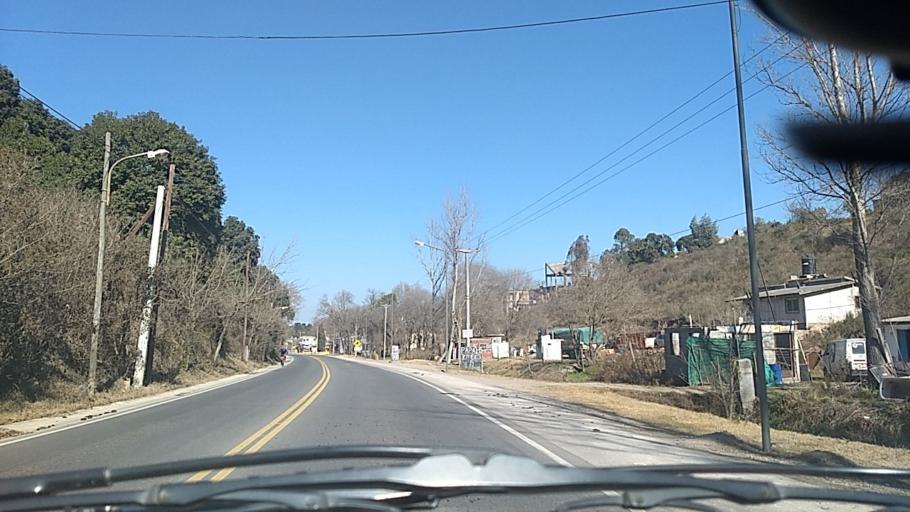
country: AR
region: Cordoba
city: Salsipuedes
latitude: -31.1016
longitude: -64.2918
